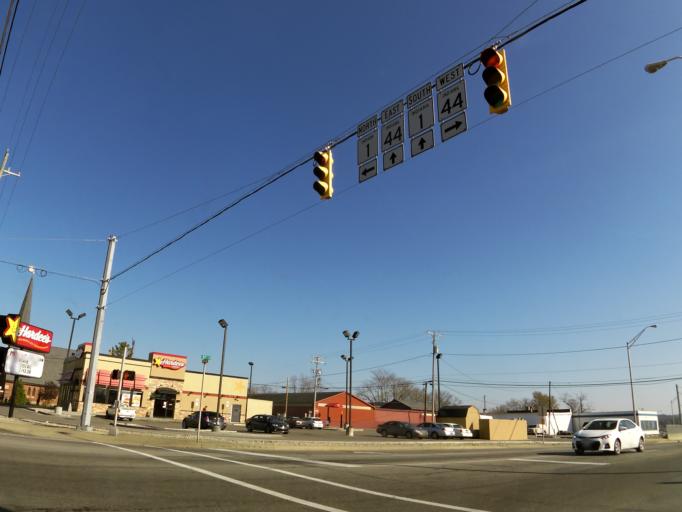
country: US
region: Indiana
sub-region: Fayette County
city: Connersville
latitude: 39.6407
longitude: -85.1381
